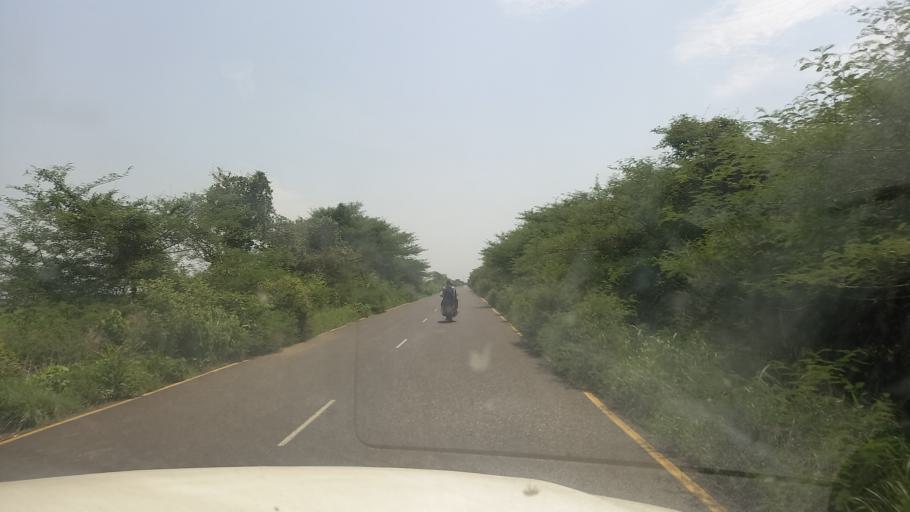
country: ET
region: Gambela
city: Gambela
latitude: 8.2843
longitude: 34.2139
